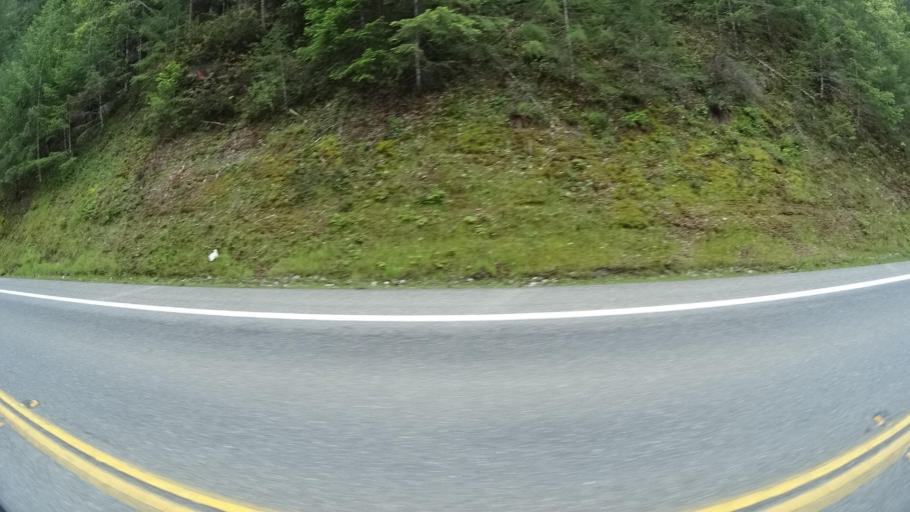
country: US
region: California
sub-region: Humboldt County
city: Willow Creek
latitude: 40.9984
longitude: -123.6424
